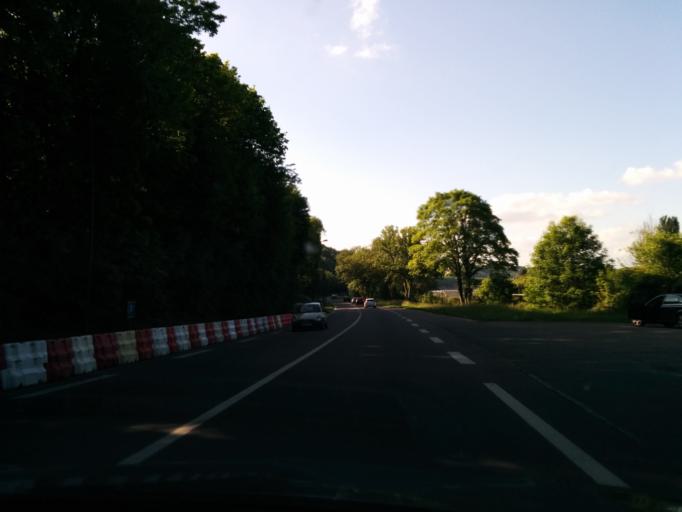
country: FR
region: Ile-de-France
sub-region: Departement des Yvelines
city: Rosny-sur-Seine
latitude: 49.0061
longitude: 1.6176
